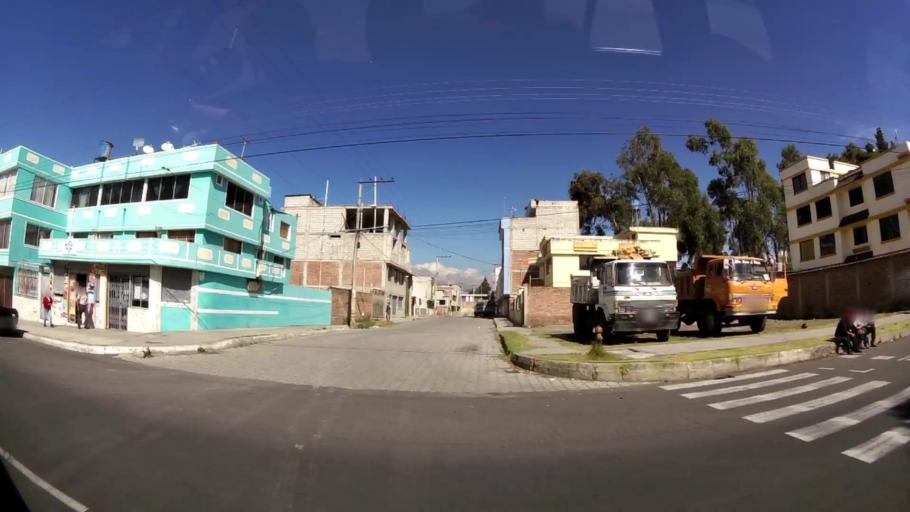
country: EC
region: Chimborazo
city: Riobamba
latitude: -1.6606
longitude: -78.6743
